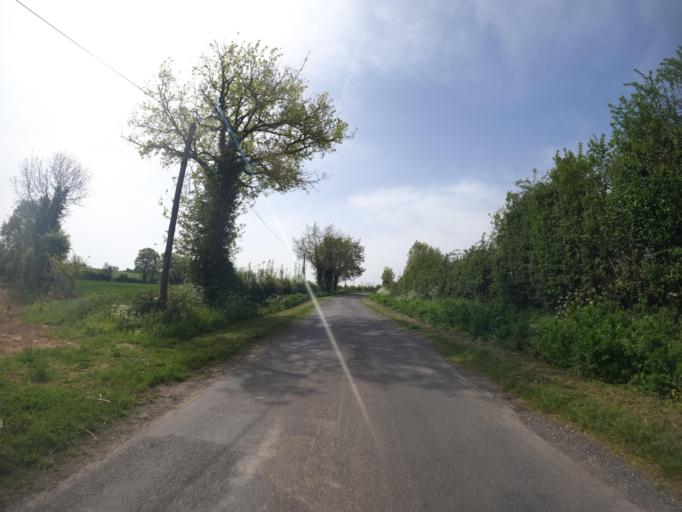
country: FR
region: Poitou-Charentes
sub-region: Departement des Deux-Sevres
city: La Chapelle-Saint-Laurent
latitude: 46.7087
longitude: -0.5051
